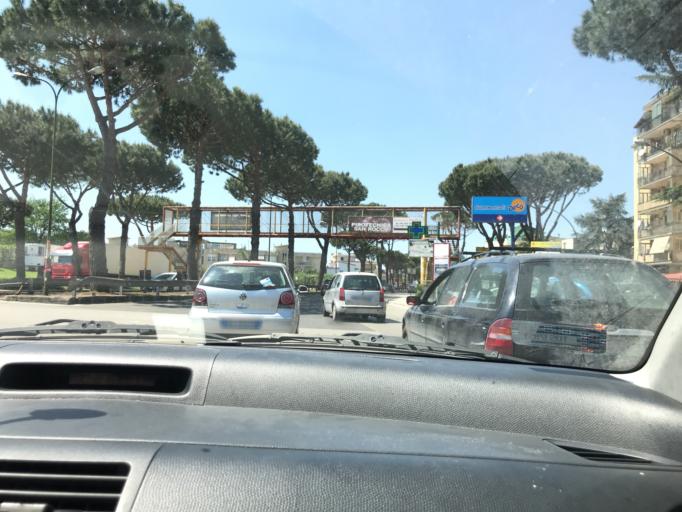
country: IT
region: Campania
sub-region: Provincia di Napoli
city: Villaricca
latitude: 40.9198
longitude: 14.1822
